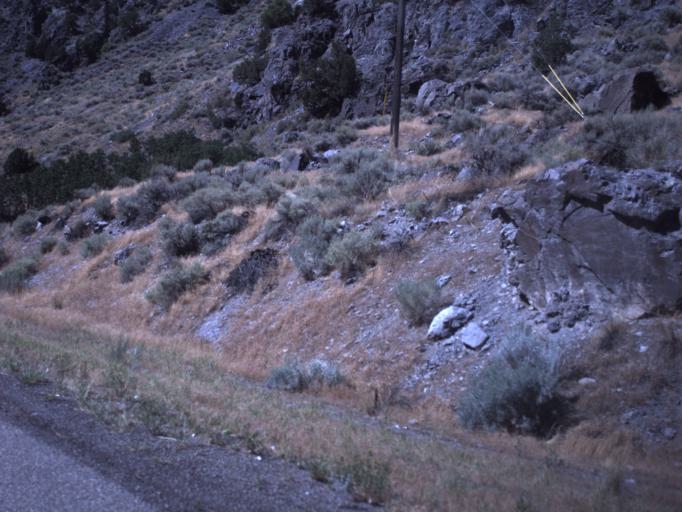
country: US
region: Utah
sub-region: Sevier County
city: Monroe
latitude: 38.5425
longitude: -112.2692
